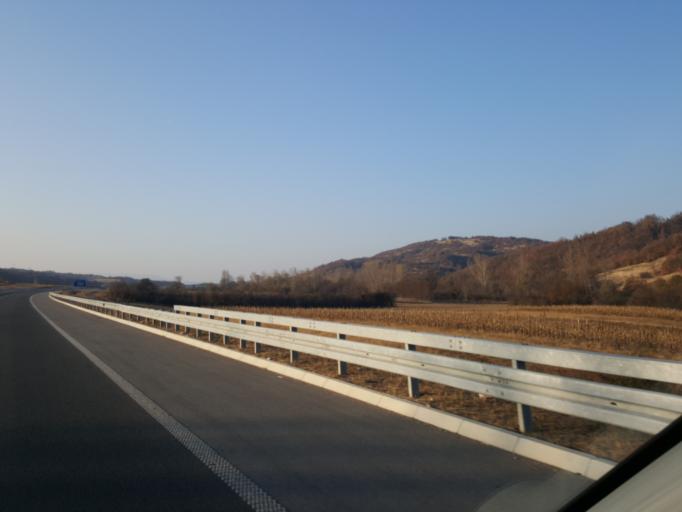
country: RS
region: Central Serbia
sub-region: Pirotski Okrug
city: Dimitrovgrad
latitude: 43.0366
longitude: 22.7159
